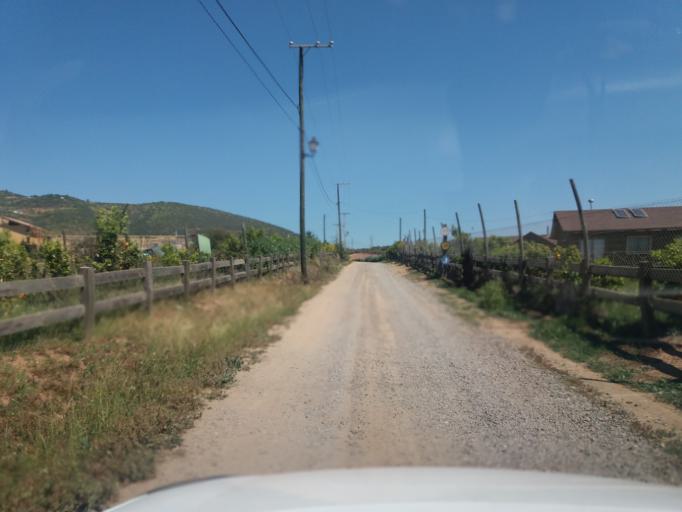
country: CL
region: Valparaiso
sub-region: Provincia de Quillota
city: Quillota
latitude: -32.9471
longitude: -71.2699
